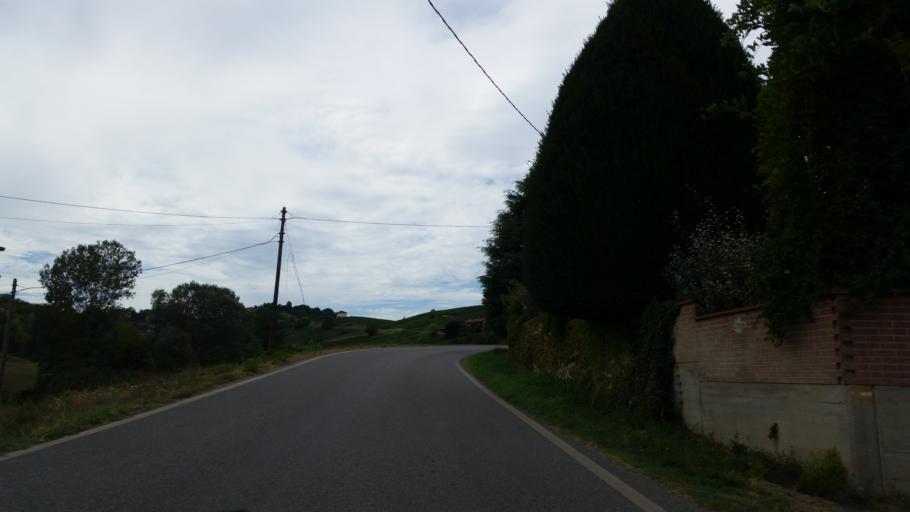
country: IT
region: Piedmont
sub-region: Provincia di Asti
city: San Martino Alfieri
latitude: 44.8215
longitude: 8.1306
